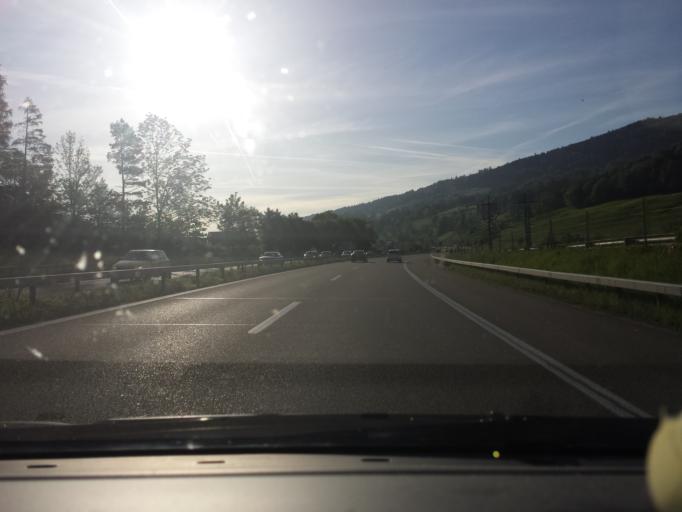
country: CH
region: Saint Gallen
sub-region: Wahlkreis Rorschach
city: Goldach
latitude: 47.4665
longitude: 9.4774
